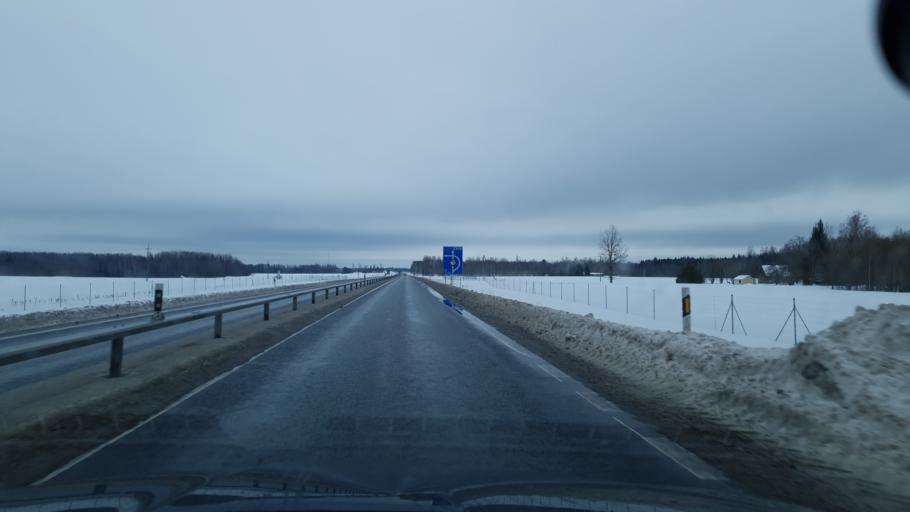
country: EE
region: Tartu
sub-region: Puhja vald
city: Puhja
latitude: 58.4469
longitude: 26.4345
